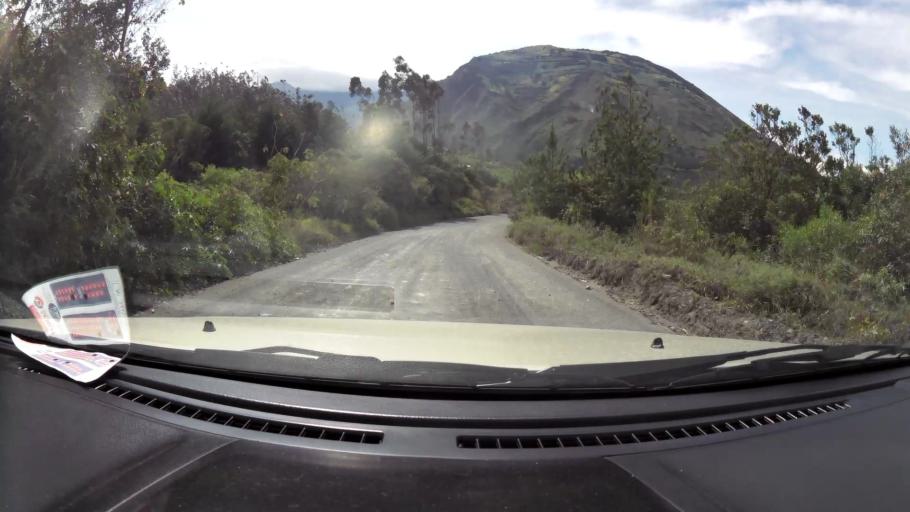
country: EC
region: Tungurahua
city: Banos
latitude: -1.4102
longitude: -78.4703
